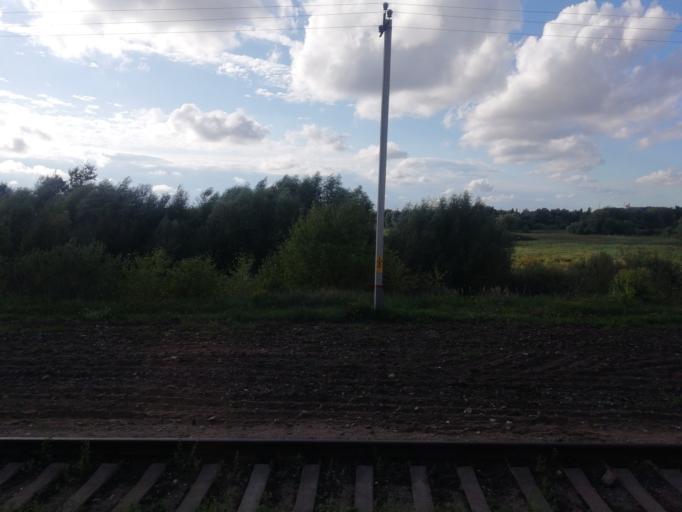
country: RU
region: Kaliningrad
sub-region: Gorod Kaliningrad
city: Kaliningrad
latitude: 54.6844
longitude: 20.4732
